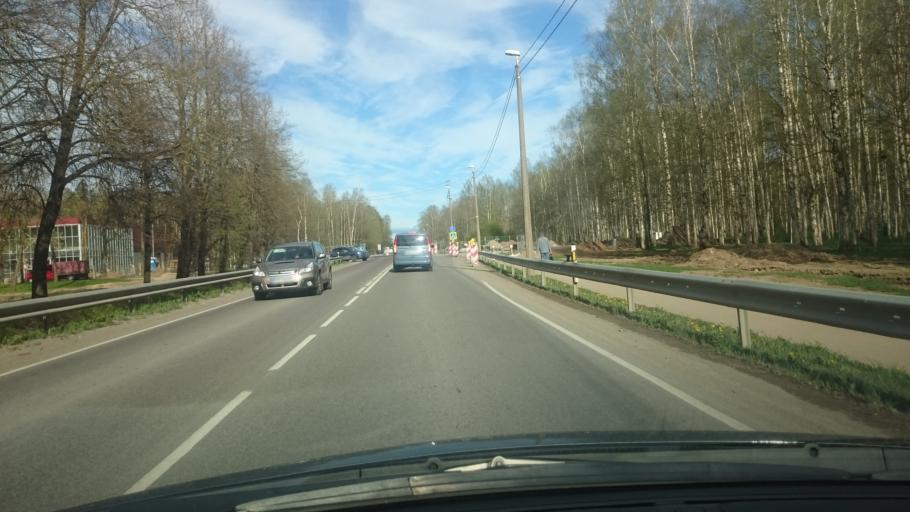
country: EE
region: Ida-Virumaa
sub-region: Sillamaee linn
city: Sillamae
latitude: 59.3910
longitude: 27.7619
